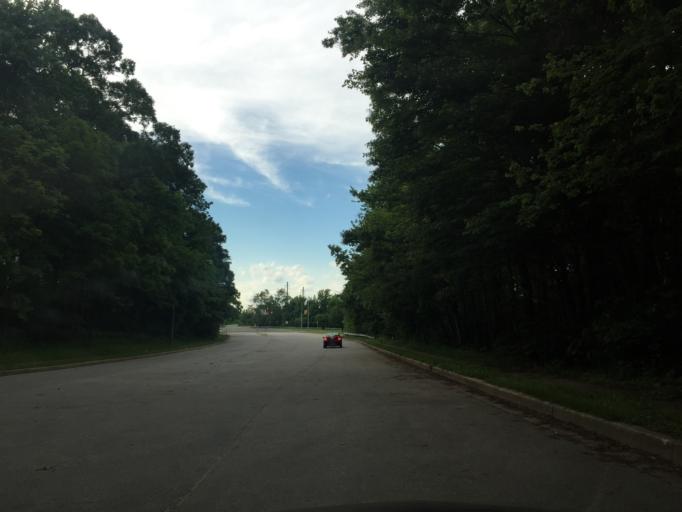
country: US
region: Maryland
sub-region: Baltimore County
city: Rossville
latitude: 39.3264
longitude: -76.4682
